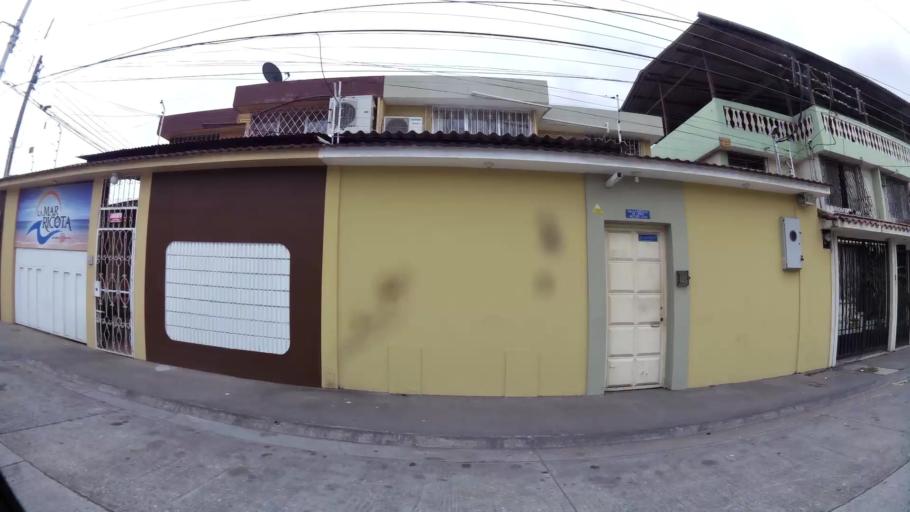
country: EC
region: Guayas
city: Eloy Alfaro
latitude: -2.1403
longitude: -79.8839
